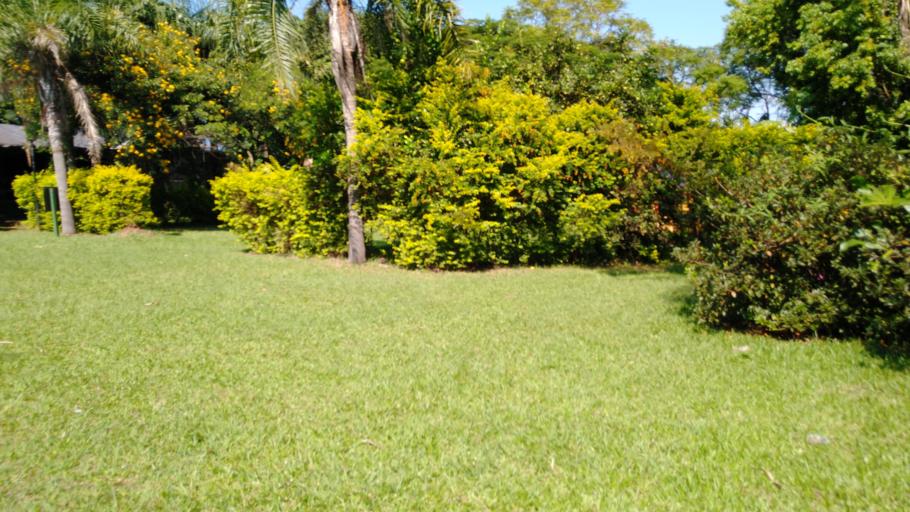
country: AR
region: Misiones
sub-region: Departamento de Capital
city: Posadas
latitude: -27.4054
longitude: -55.9778
